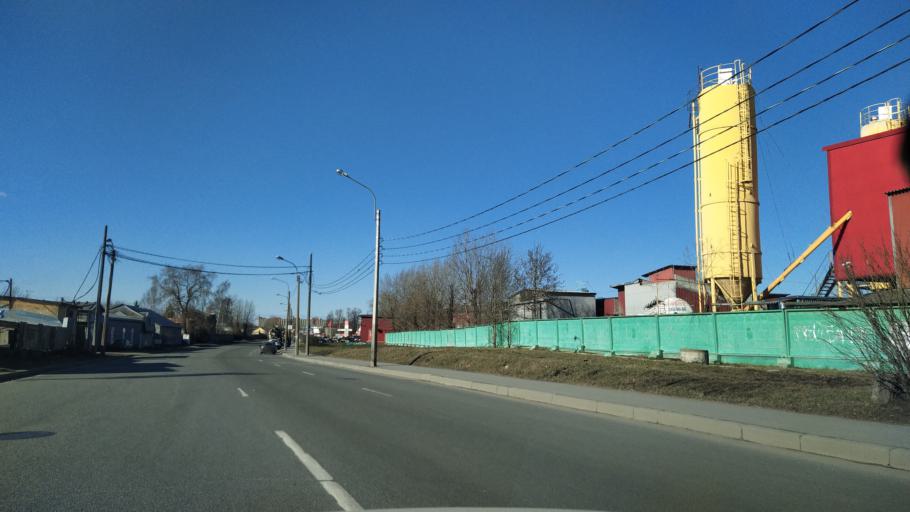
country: RU
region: St.-Petersburg
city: Centralniy
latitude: 59.9064
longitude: 30.3789
